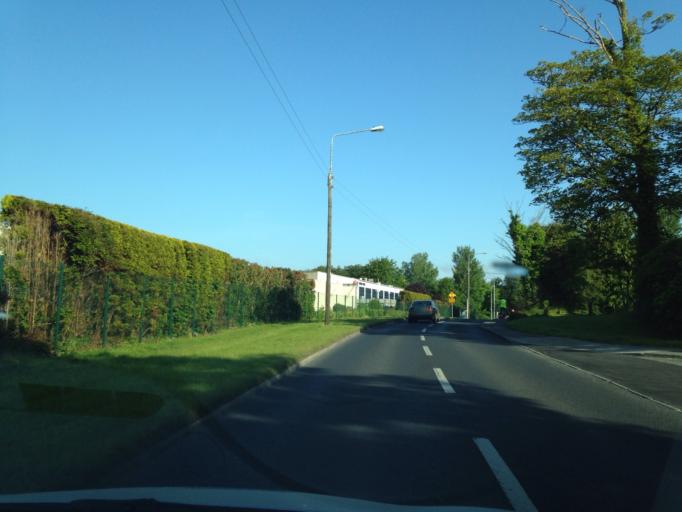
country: IE
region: Connaught
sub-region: County Galway
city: Gaillimh
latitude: 53.2849
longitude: -9.0218
